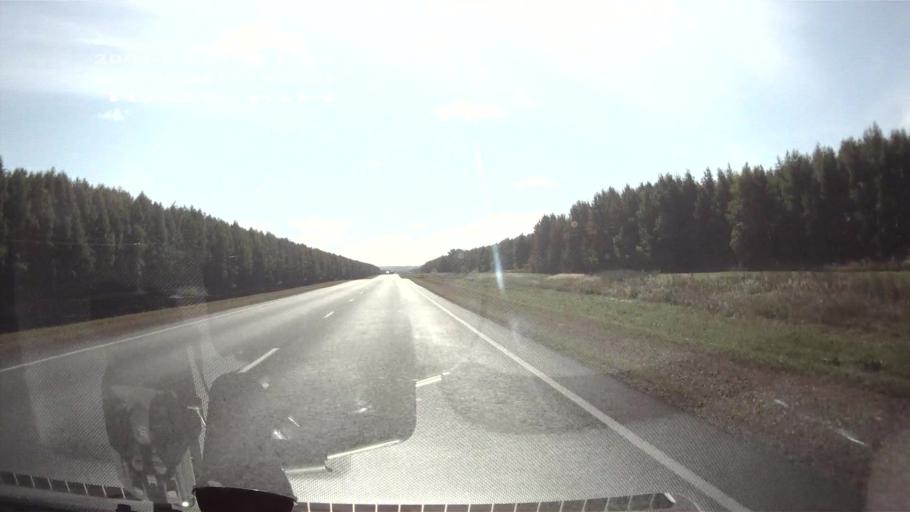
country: RU
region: Ulyanovsk
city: Tsil'na
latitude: 54.5497
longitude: 47.9442
